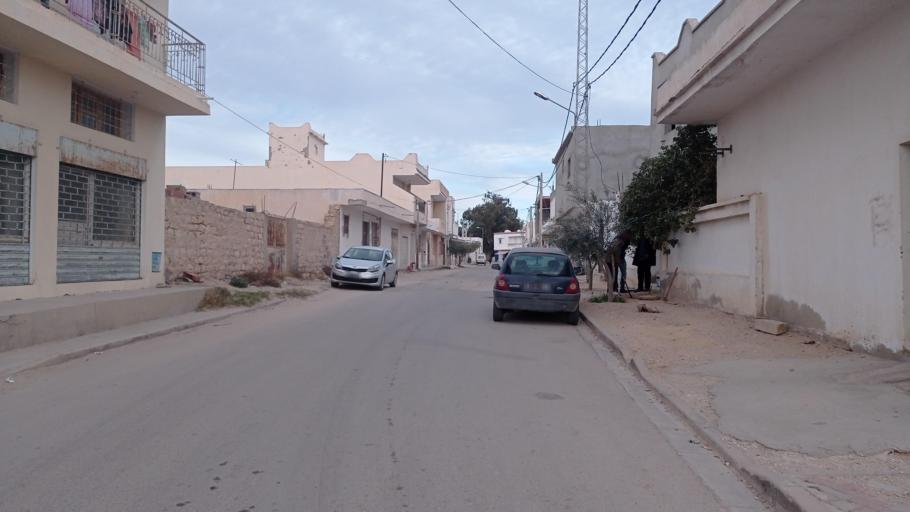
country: TN
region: Qabis
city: Gabes
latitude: 33.8388
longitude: 10.1142
